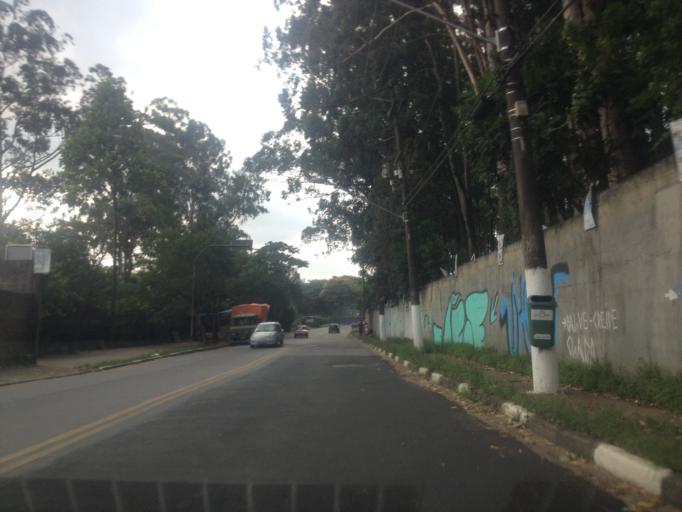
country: BR
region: Sao Paulo
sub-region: Diadema
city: Diadema
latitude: -23.7294
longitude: -46.7173
